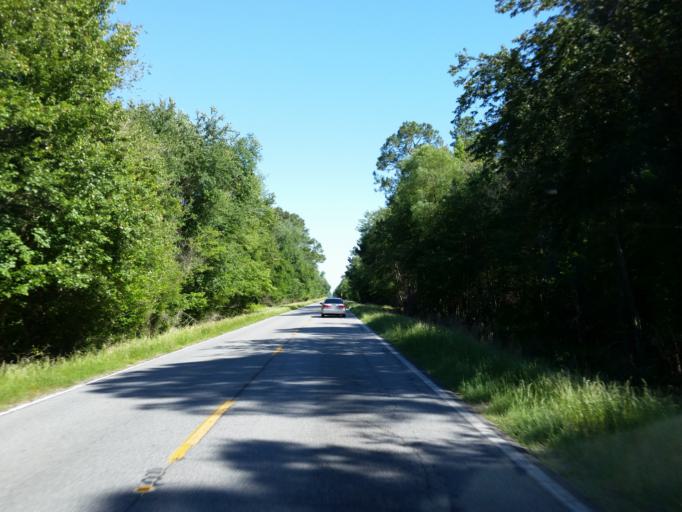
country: US
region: Georgia
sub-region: Echols County
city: Statenville
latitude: 30.6658
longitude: -83.1606
